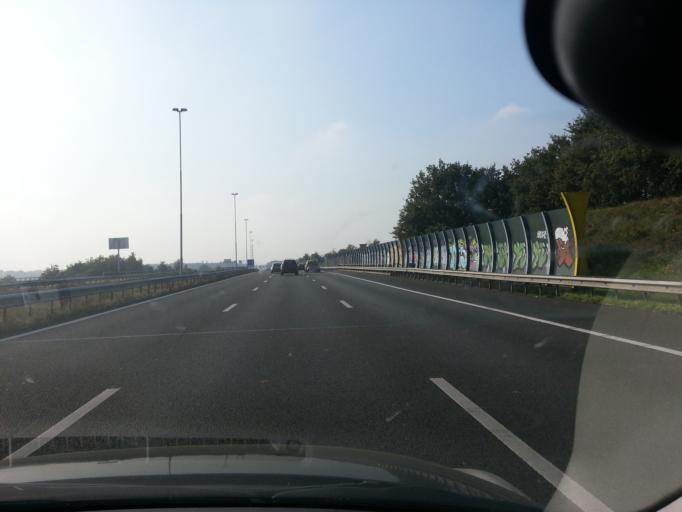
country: NL
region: North Brabant
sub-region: Gemeente Goirle
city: Goirle
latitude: 51.5400
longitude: 5.0348
